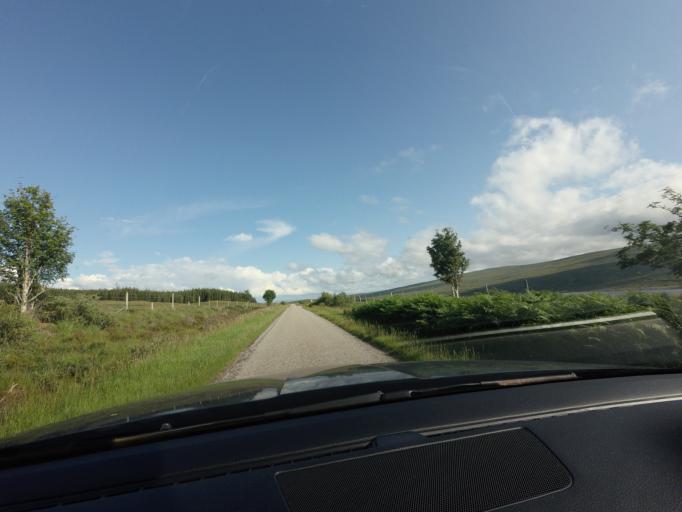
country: GB
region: Scotland
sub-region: Highland
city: Ullapool
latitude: 58.1684
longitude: -4.6891
